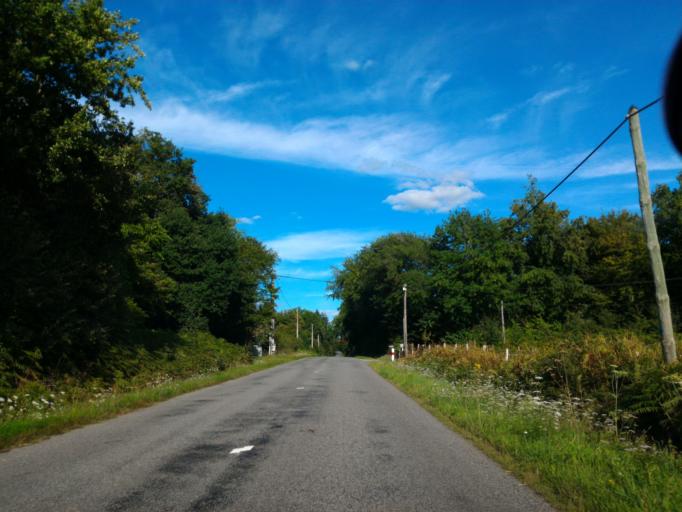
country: FR
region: Poitou-Charentes
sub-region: Departement de la Charente
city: Brigueuil
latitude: 45.9868
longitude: 0.9203
